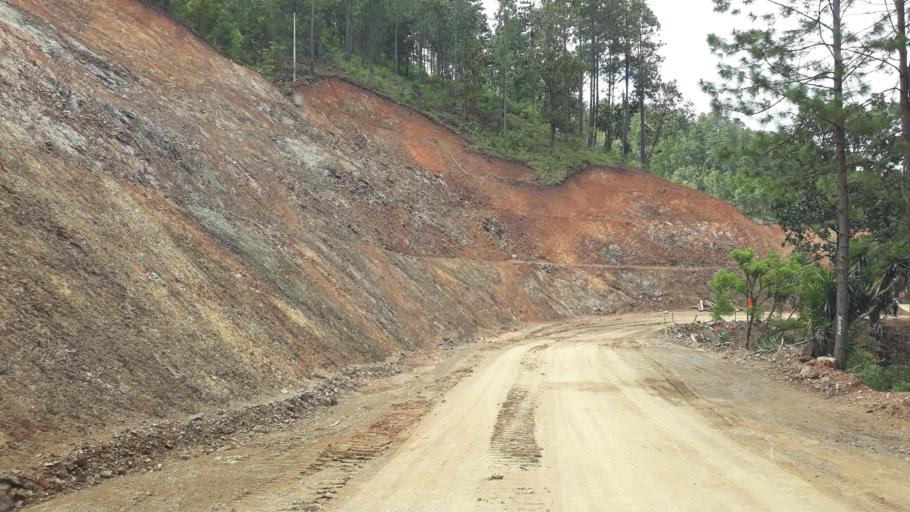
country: HN
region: El Paraiso
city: Santa Cruz
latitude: 13.7616
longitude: -86.6488
